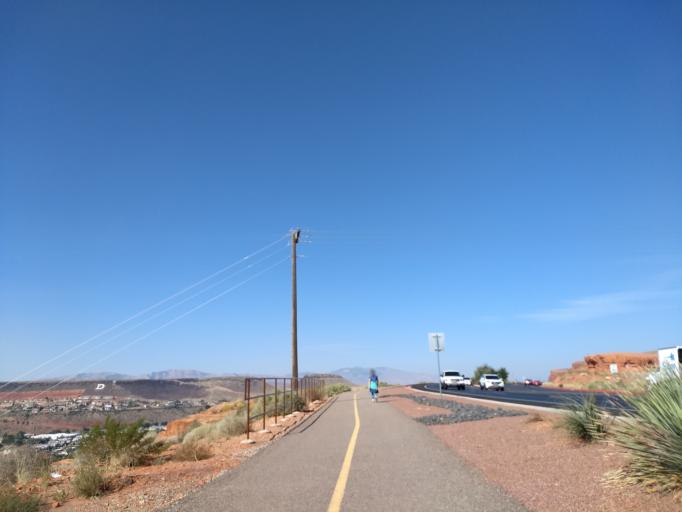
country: US
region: Utah
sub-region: Washington County
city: Saint George
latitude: 37.1133
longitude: -113.5754
